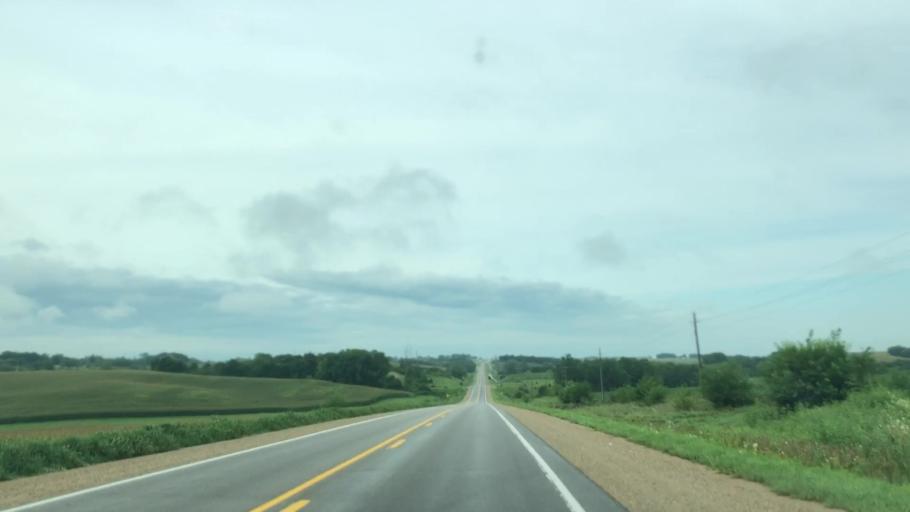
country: US
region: Iowa
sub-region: Marshall County
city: Marshalltown
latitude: 42.0075
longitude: -92.9526
